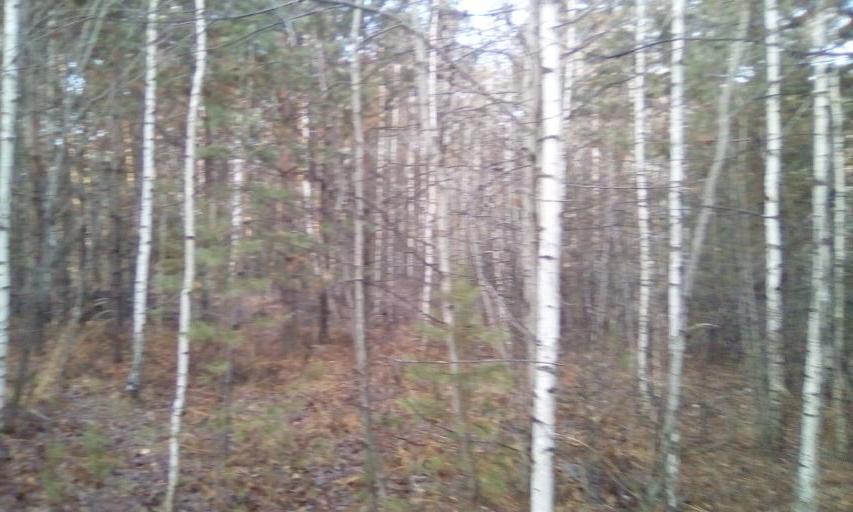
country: RU
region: Chelyabinsk
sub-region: Gorod Chelyabinsk
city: Chelyabinsk
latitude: 55.1618
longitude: 61.3531
